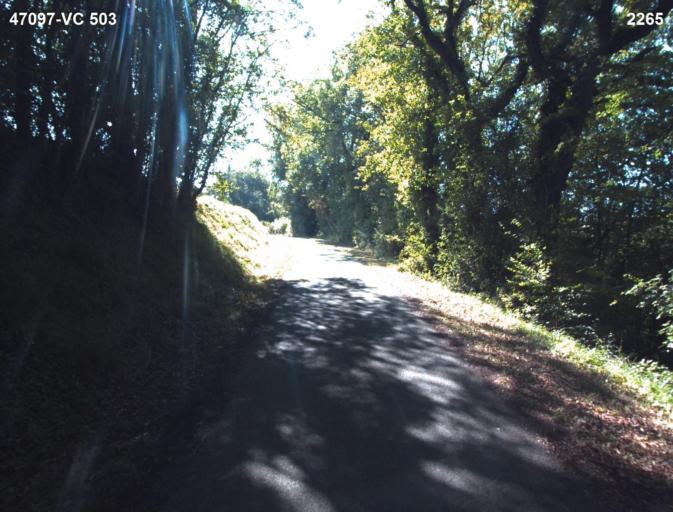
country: FR
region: Aquitaine
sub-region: Departement du Lot-et-Garonne
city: Port-Sainte-Marie
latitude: 44.2101
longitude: 0.3681
